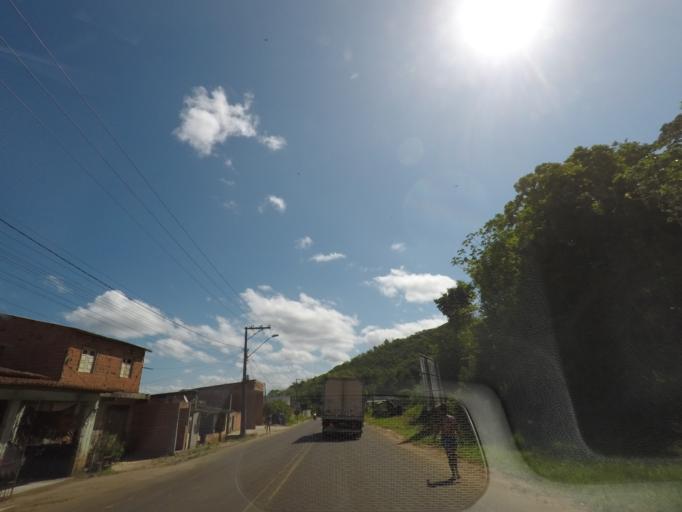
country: BR
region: Bahia
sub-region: Itubera
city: Itubera
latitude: -13.7457
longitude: -39.1518
